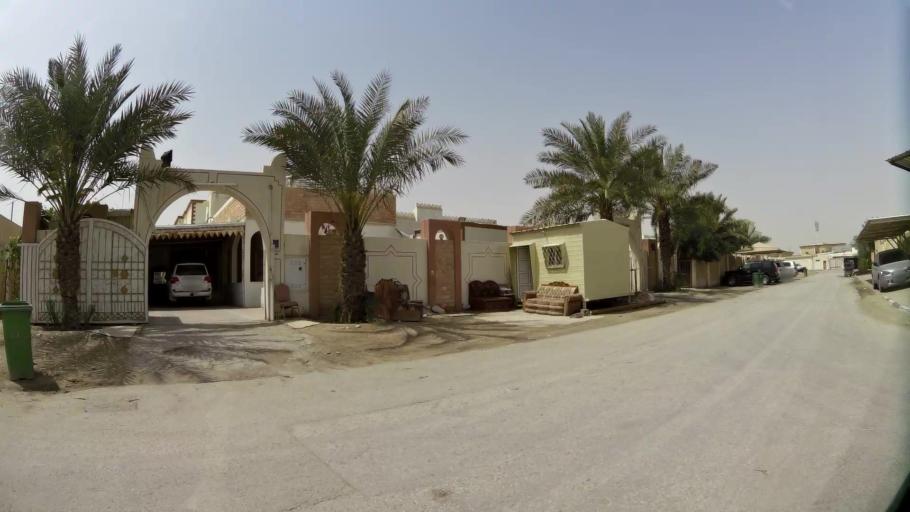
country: QA
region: Baladiyat ar Rayyan
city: Ar Rayyan
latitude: 25.2323
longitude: 51.4190
